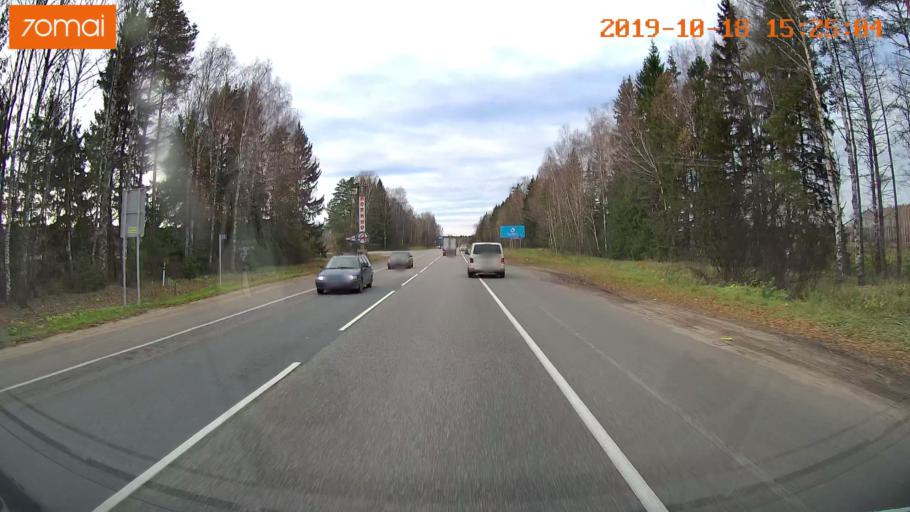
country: RU
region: Vladimir
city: Anopino
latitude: 55.7387
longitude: 40.7125
